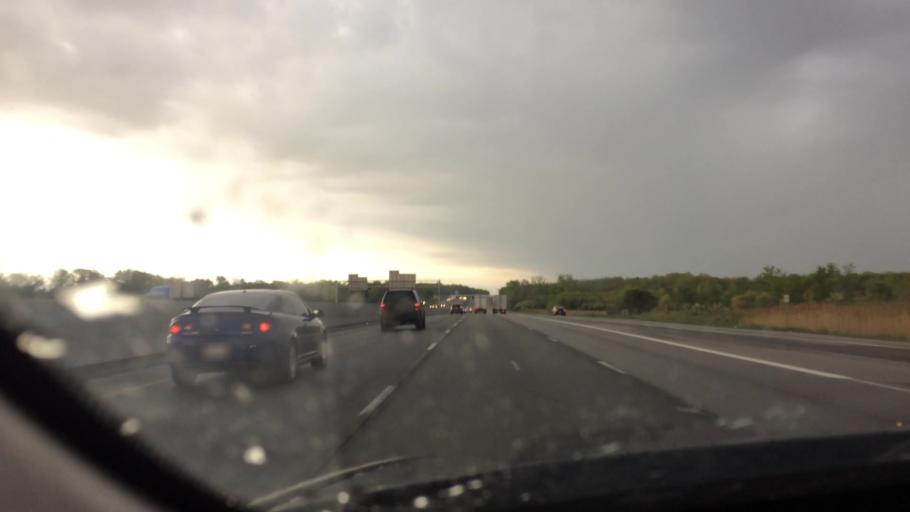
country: US
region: Ohio
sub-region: Wood County
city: North Baltimore
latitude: 41.1363
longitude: -83.6591
